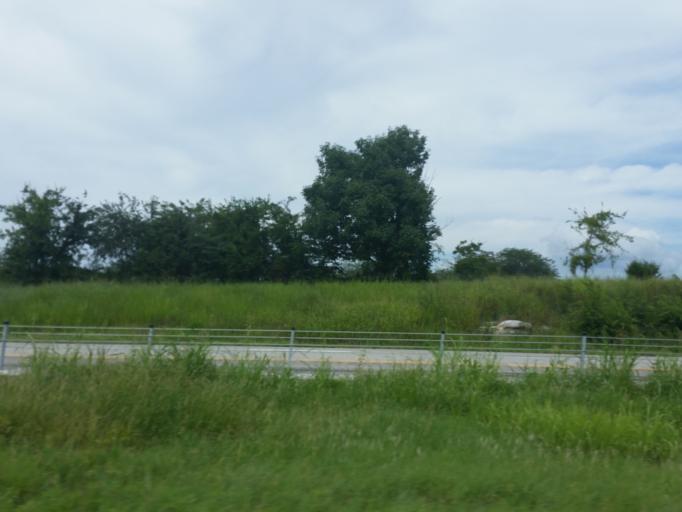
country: US
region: Kentucky
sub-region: Trigg County
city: Cadiz
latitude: 36.9163
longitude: -87.7906
